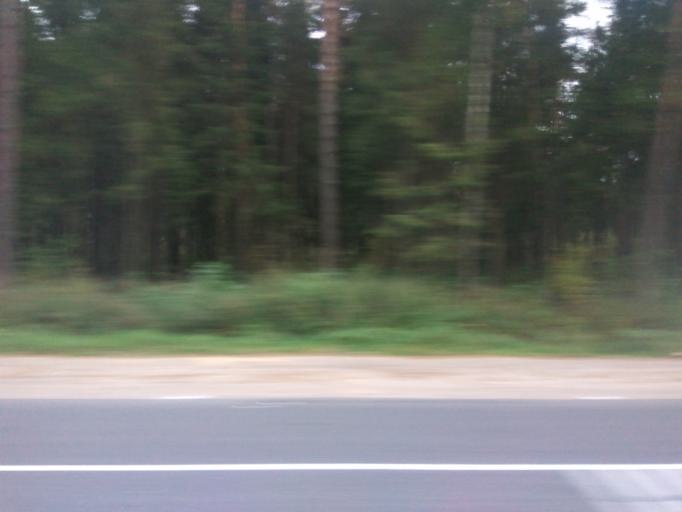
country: RU
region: Moskovskaya
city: Krasnoarmeysk
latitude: 56.0313
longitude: 38.1860
